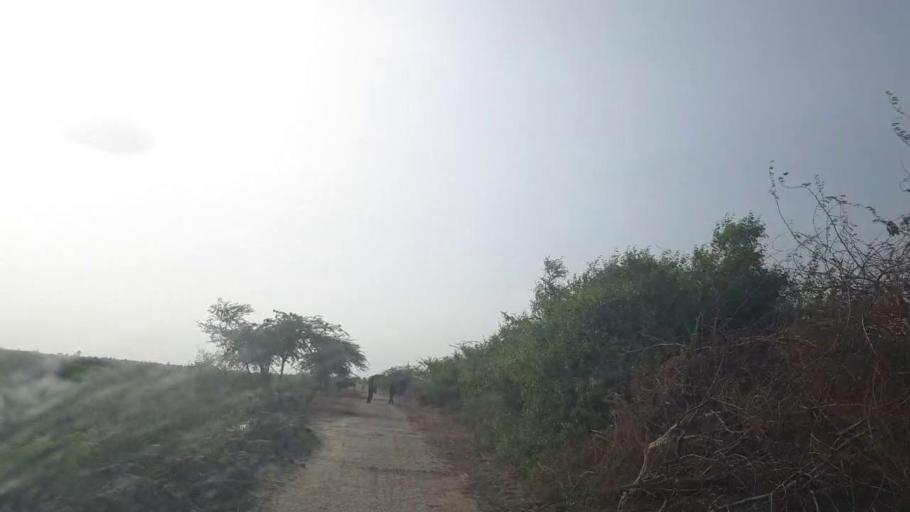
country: PK
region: Sindh
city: Tando Bago
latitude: 24.7617
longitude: 69.0804
